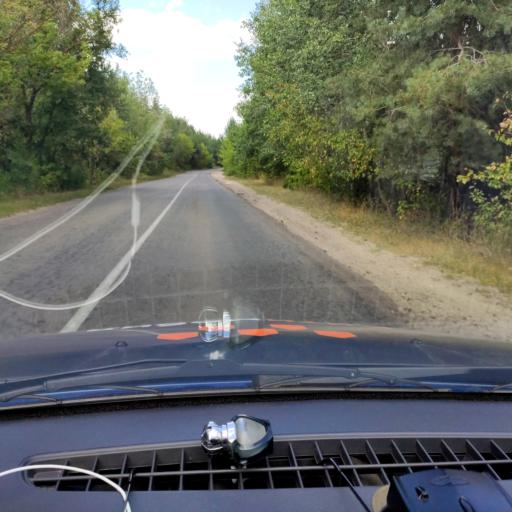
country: RU
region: Voronezj
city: Somovo
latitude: 51.7126
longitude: 39.3673
